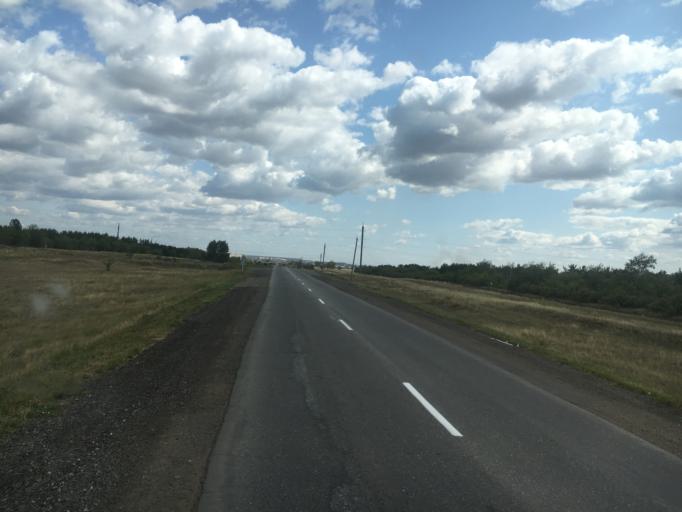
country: KZ
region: Qostanay
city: Rudnyy
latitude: 52.9372
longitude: 63.0237
